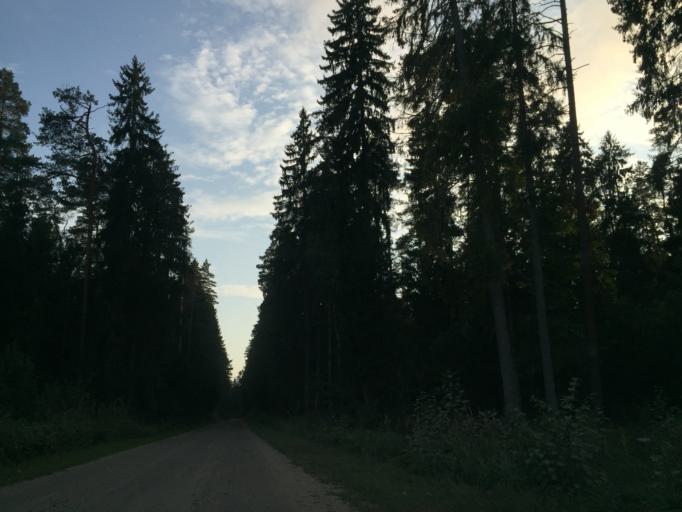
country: LV
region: Baldone
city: Baldone
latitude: 56.7550
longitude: 24.4075
